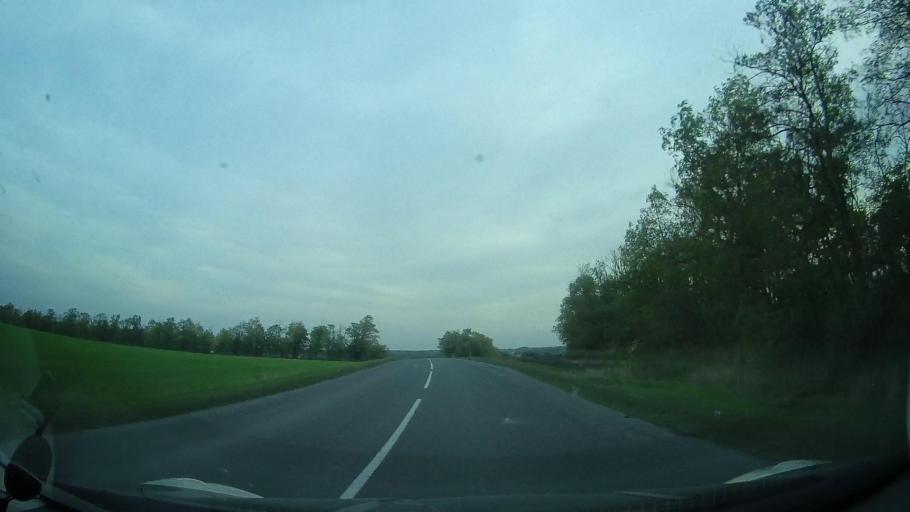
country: RU
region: Rostov
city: Kirovskaya
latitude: 47.0416
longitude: 39.9773
